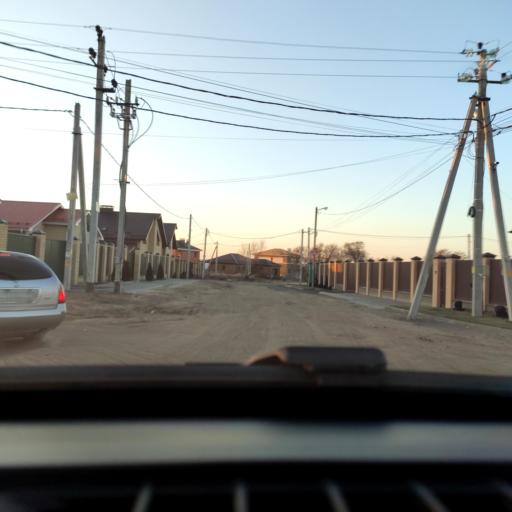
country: RU
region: Voronezj
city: Podgornoye
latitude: 51.7257
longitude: 39.1351
